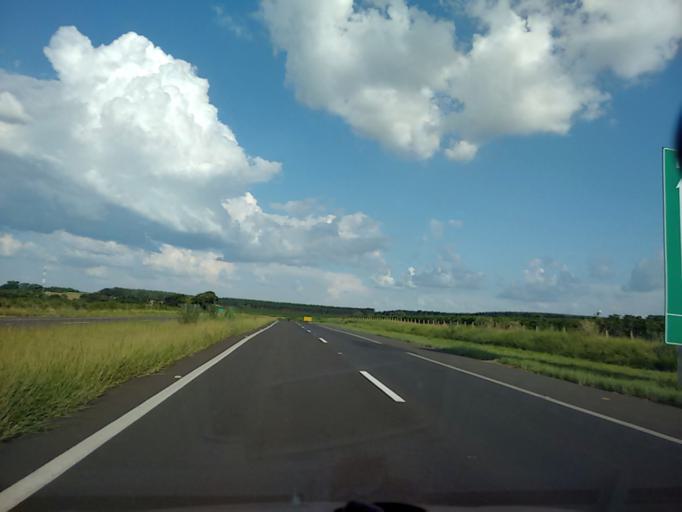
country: BR
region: Sao Paulo
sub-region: Duartina
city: Duartina
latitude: -22.3300
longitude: -49.4615
